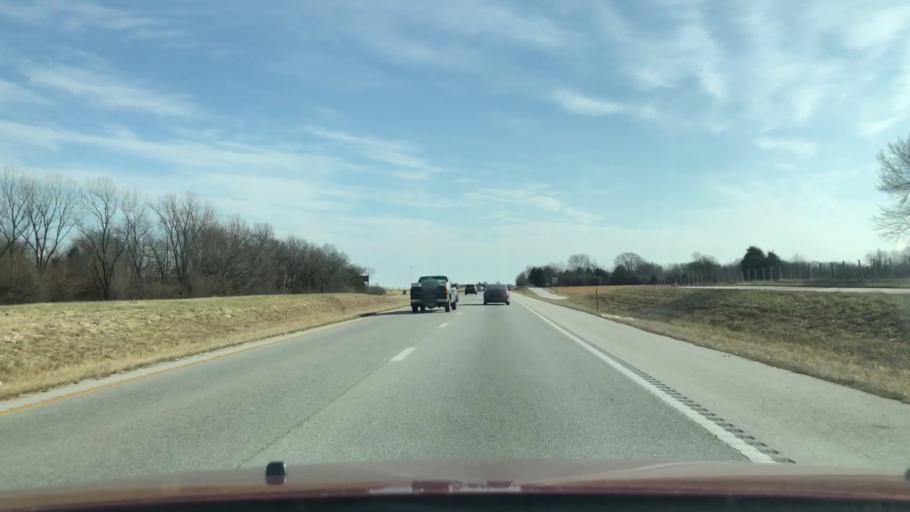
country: US
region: Missouri
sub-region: Webster County
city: Rogersville
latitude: 37.1182
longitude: -93.1006
